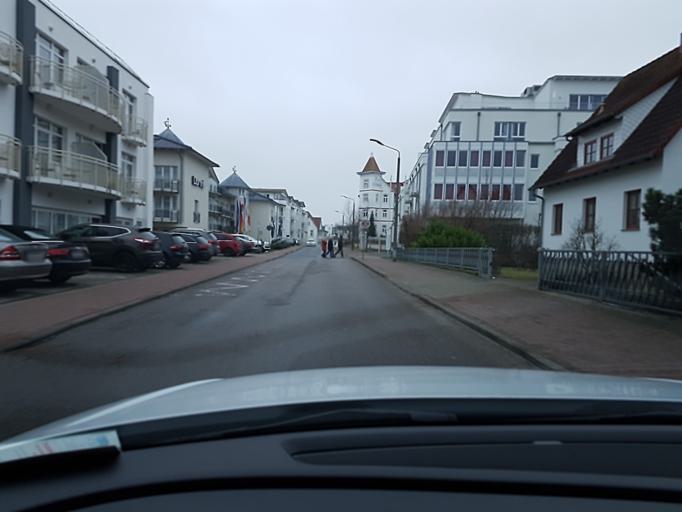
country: DE
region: Mecklenburg-Vorpommern
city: Ostseebad Binz
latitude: 54.4070
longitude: 13.6048
